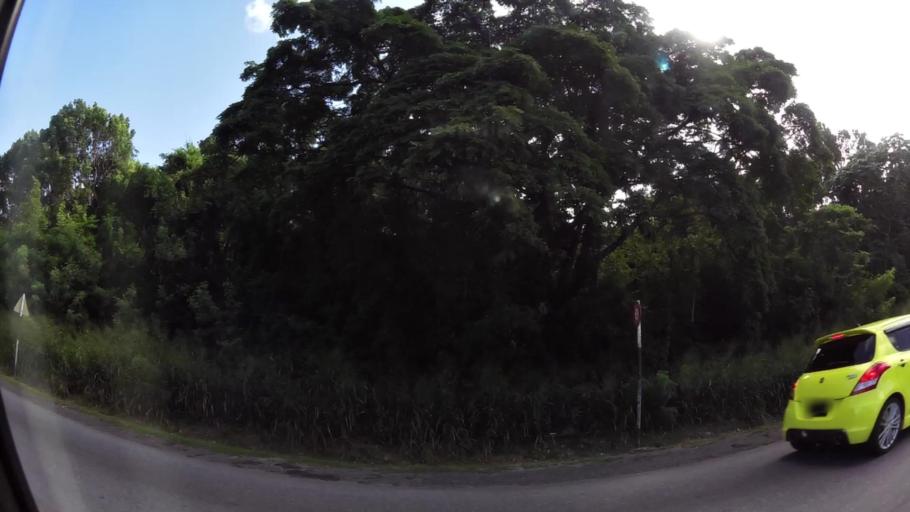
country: BB
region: Saint James
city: Holetown
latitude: 13.1943
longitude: -59.6123
